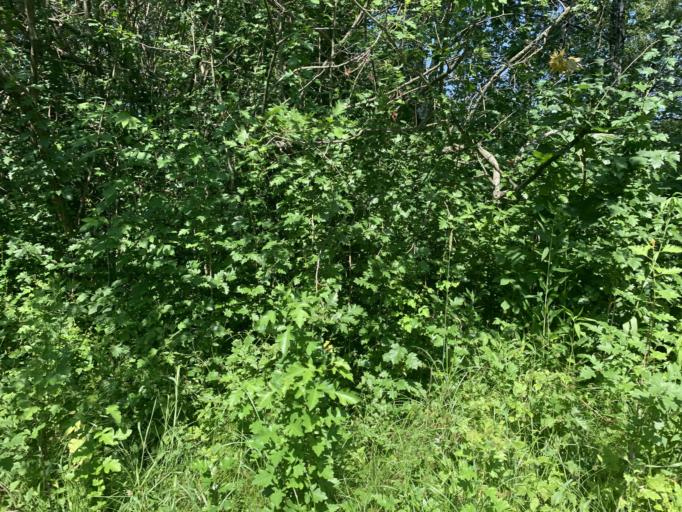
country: RU
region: Moskovskaya
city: Mamontovka
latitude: 55.9686
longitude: 37.8181
